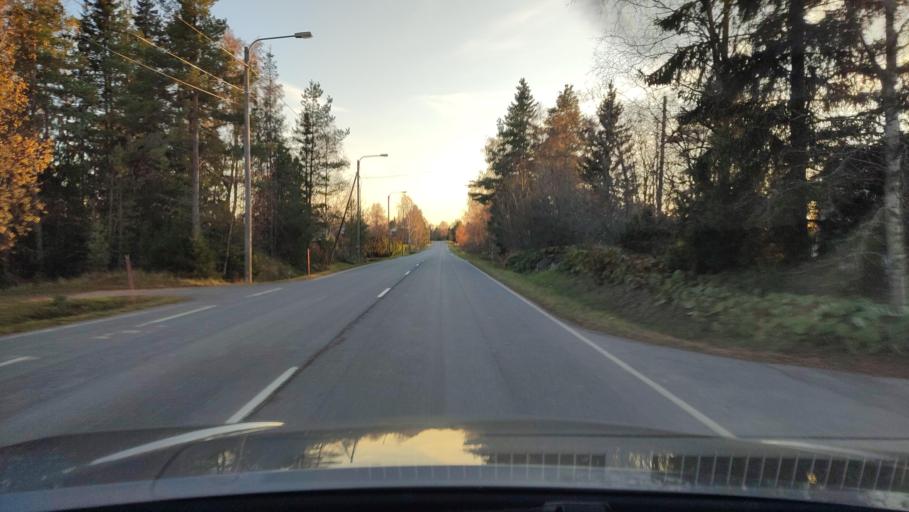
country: FI
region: Ostrobothnia
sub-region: Sydosterbotten
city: Naerpes
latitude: 62.4986
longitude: 21.3478
